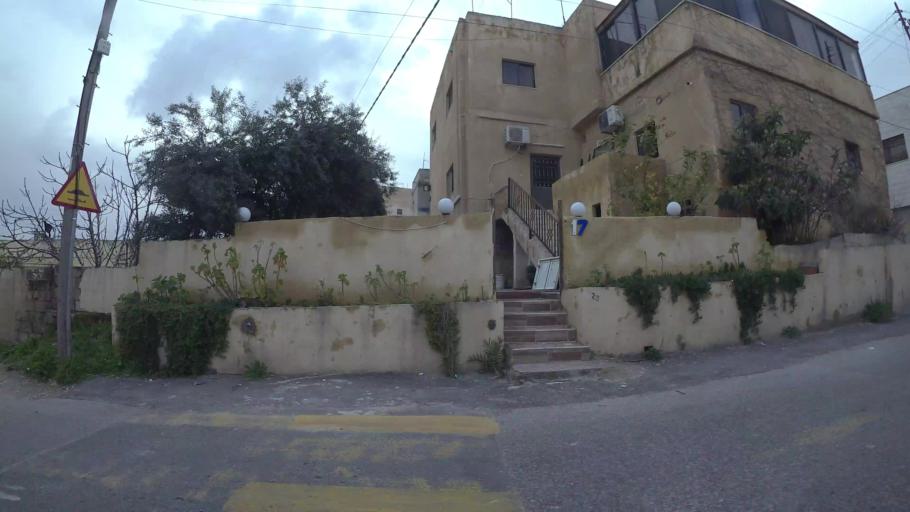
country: JO
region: Amman
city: Umm as Summaq
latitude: 31.8854
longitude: 35.8687
